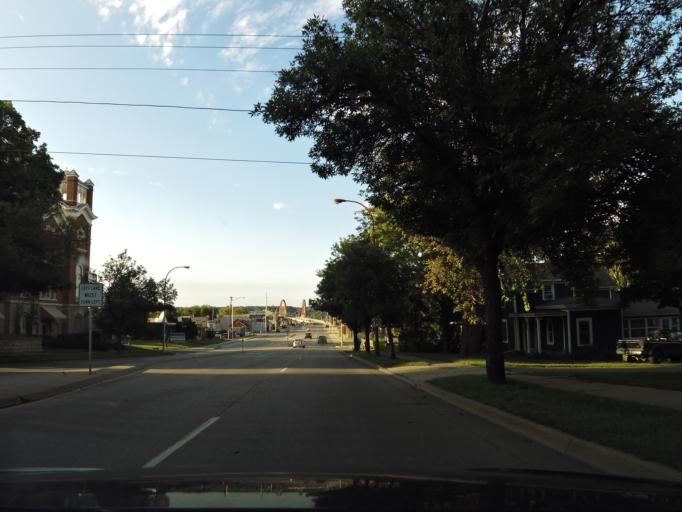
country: US
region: Minnesota
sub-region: Dakota County
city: Hastings
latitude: 44.7395
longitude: -92.8525
